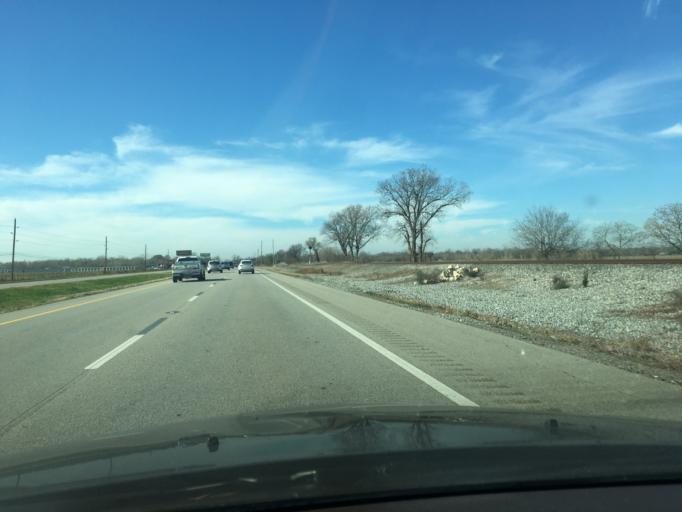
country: US
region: Texas
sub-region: Fort Bend County
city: Pecan Grove
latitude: 29.5980
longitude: -95.7234
